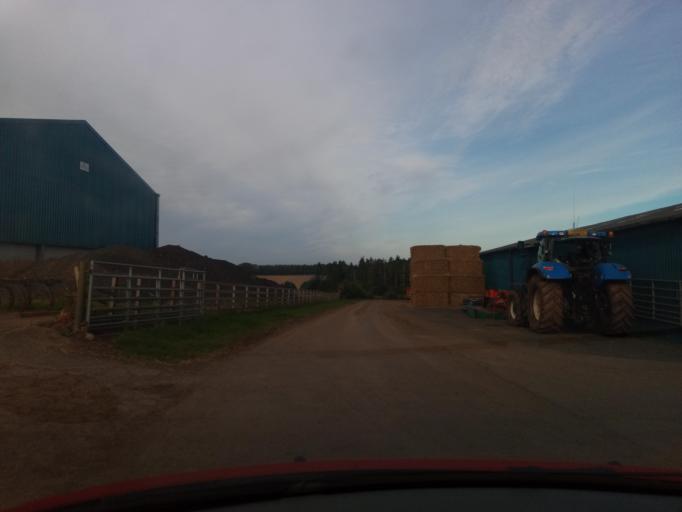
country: GB
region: Scotland
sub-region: The Scottish Borders
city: Kelso
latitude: 55.5811
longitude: -2.3691
